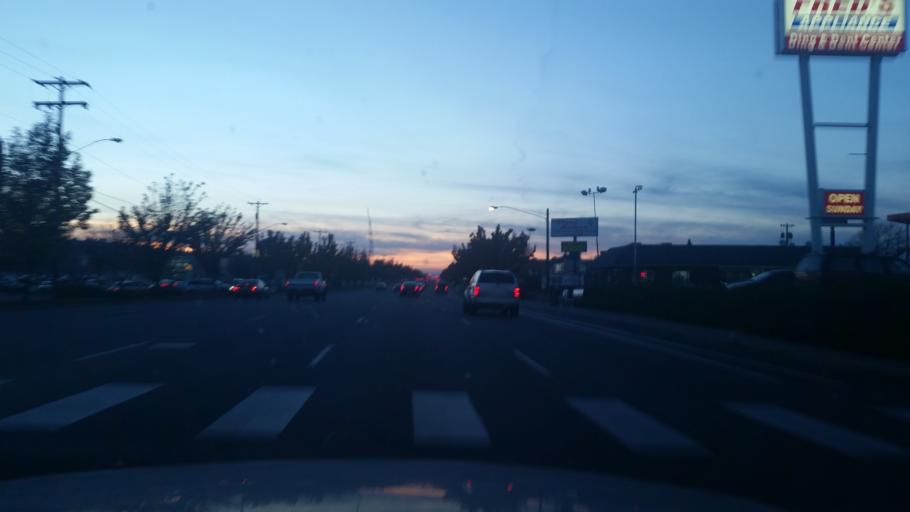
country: US
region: Washington
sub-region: Spokane County
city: Dishman
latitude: 47.6572
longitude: -117.2614
